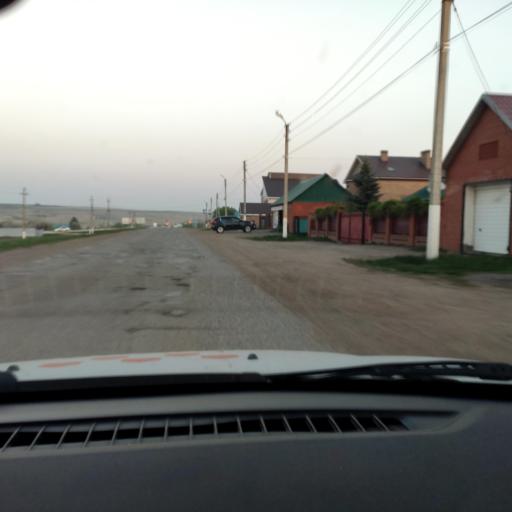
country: RU
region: Bashkortostan
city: Karmaskaly
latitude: 54.3616
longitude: 56.1595
